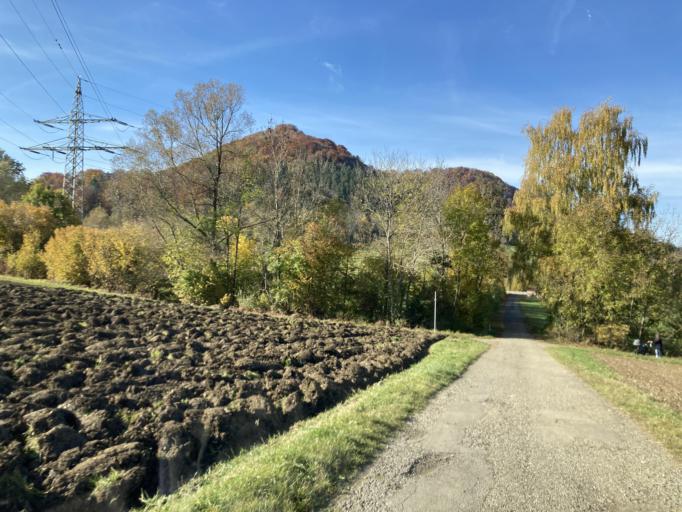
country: DE
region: Baden-Wuerttemberg
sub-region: Tuebingen Region
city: Mossingen
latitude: 48.3789
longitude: 9.0956
